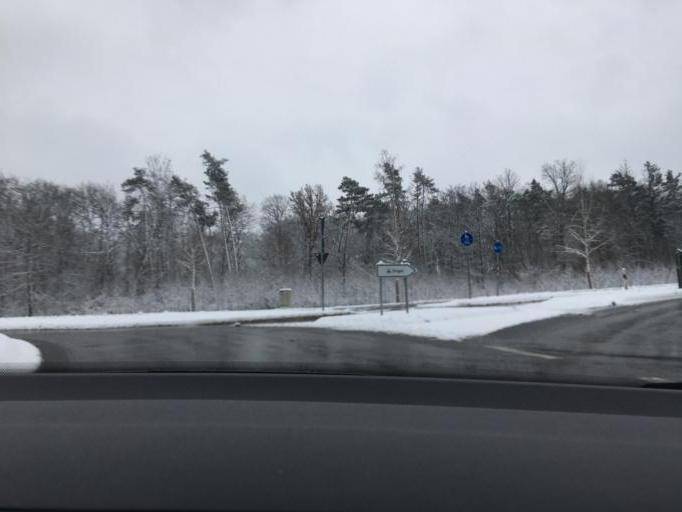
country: DE
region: Baden-Wuerttemberg
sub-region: Freiburg Region
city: Singen
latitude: 47.7610
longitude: 8.8782
